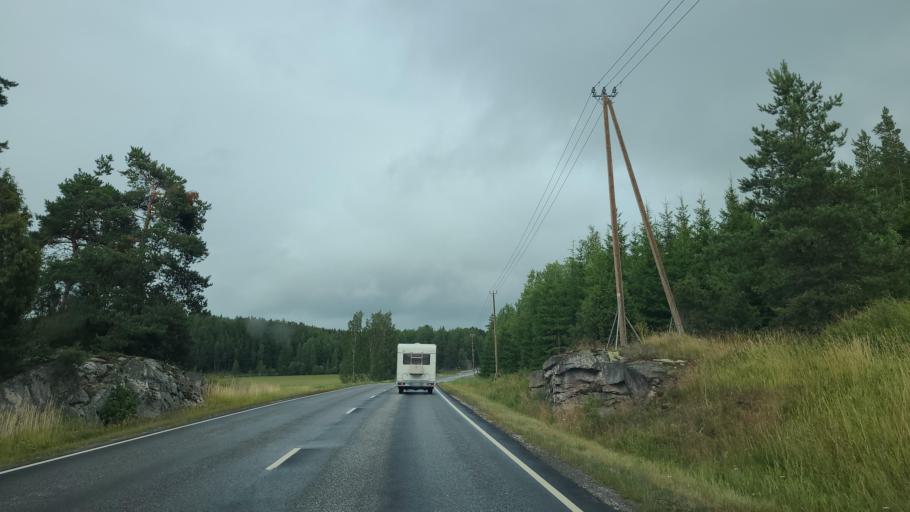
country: FI
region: Varsinais-Suomi
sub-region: Turku
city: Sauvo
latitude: 60.2625
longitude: 22.6448
